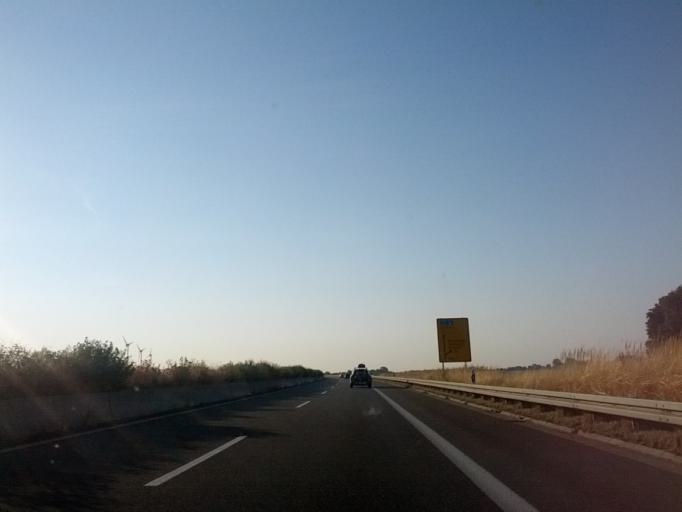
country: DE
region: Mecklenburg-Vorpommern
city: Zarrendorf
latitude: 54.2467
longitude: 13.1330
